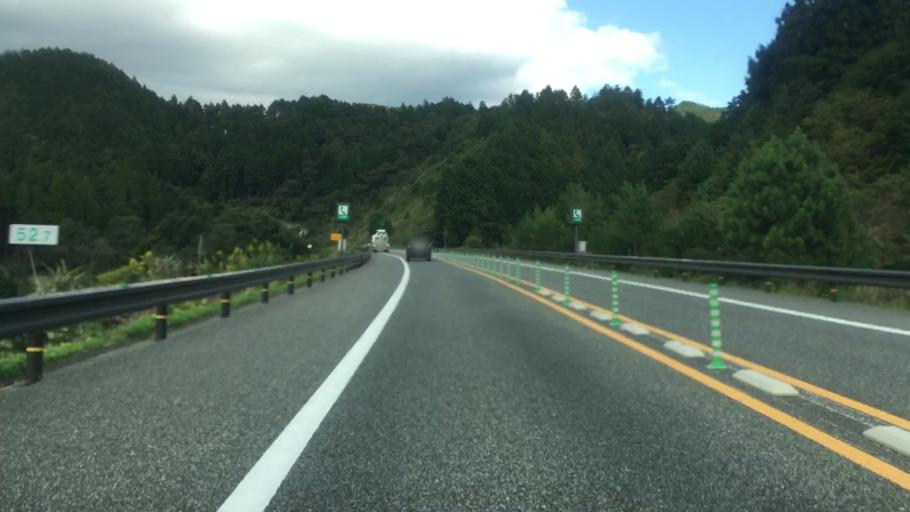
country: JP
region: Kyoto
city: Fukuchiyama
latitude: 35.2574
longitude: 135.0127
